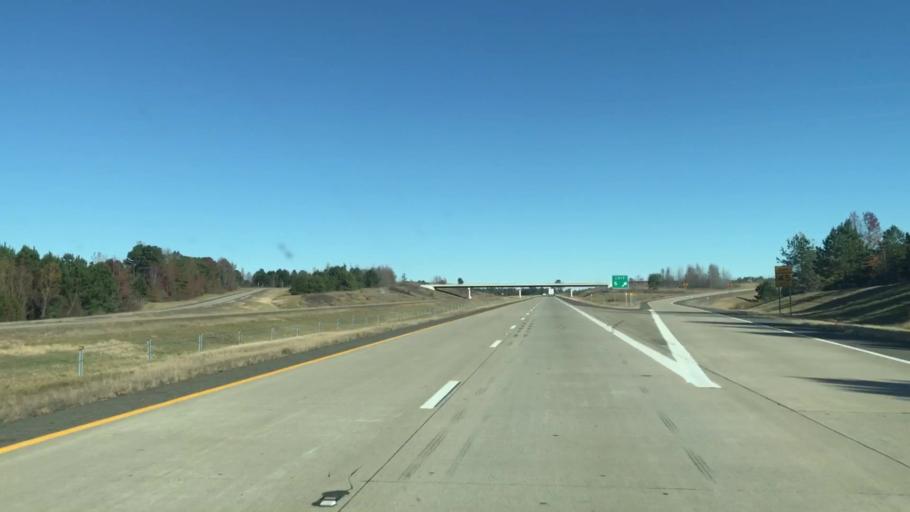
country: US
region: Texas
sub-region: Cass County
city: Queen City
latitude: 33.1158
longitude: -93.8939
